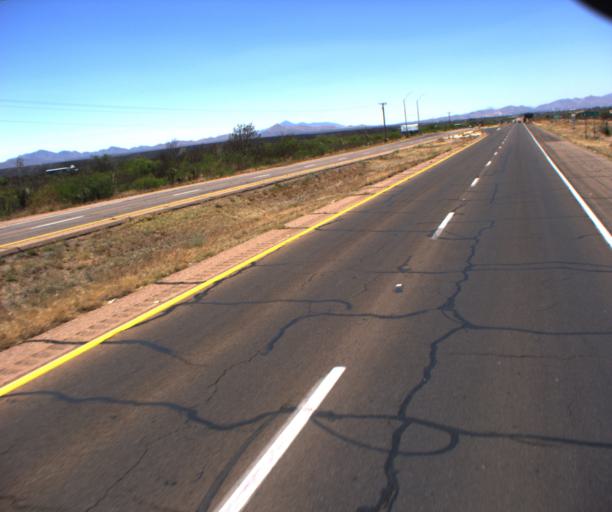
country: US
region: Arizona
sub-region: Cochise County
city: Pirtleville
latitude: 31.3515
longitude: -109.5700
